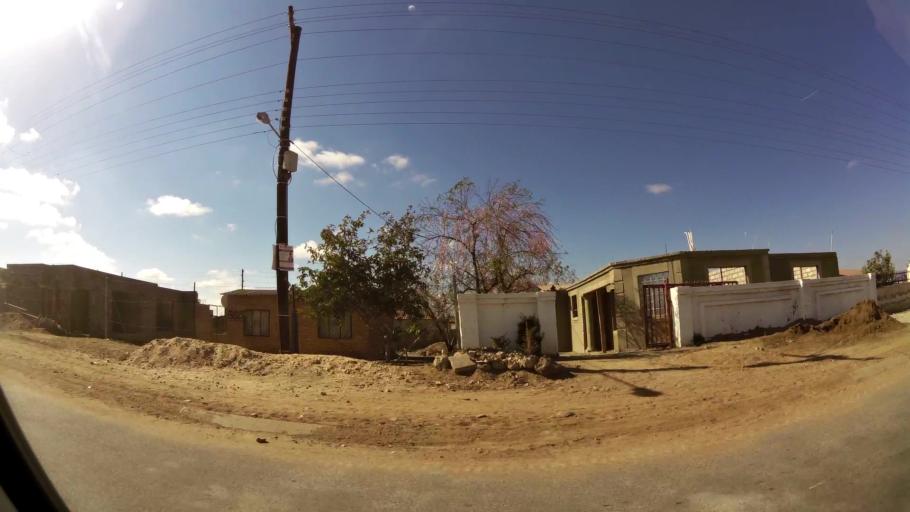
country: ZA
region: Limpopo
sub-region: Capricorn District Municipality
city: Polokwane
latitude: -23.8581
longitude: 29.3964
